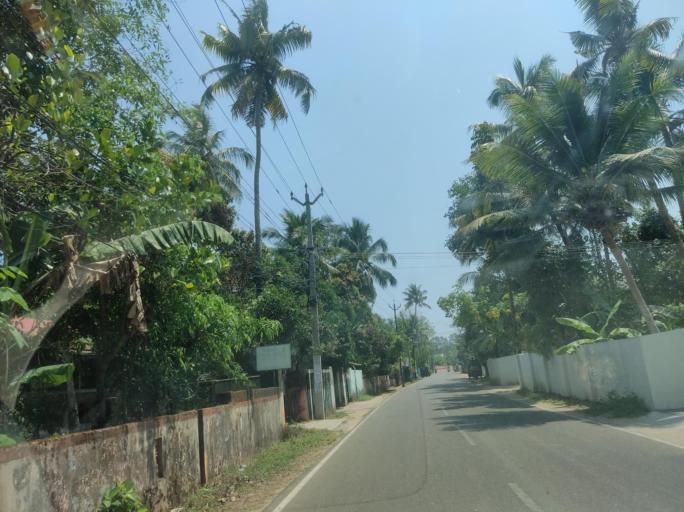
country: IN
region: Kerala
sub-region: Alappuzha
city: Kutiatodu
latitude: 9.8266
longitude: 76.2983
